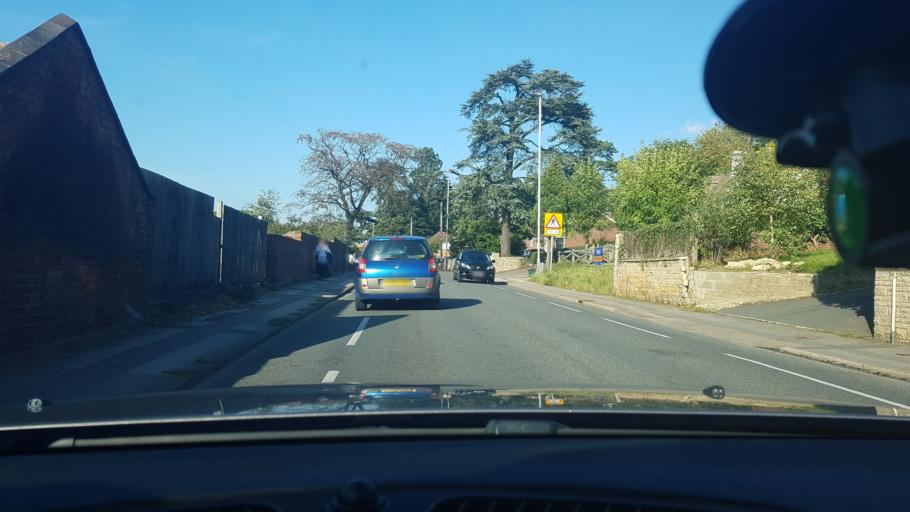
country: GB
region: England
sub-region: Gloucestershire
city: Gloucester
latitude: 51.8351
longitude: -2.2438
